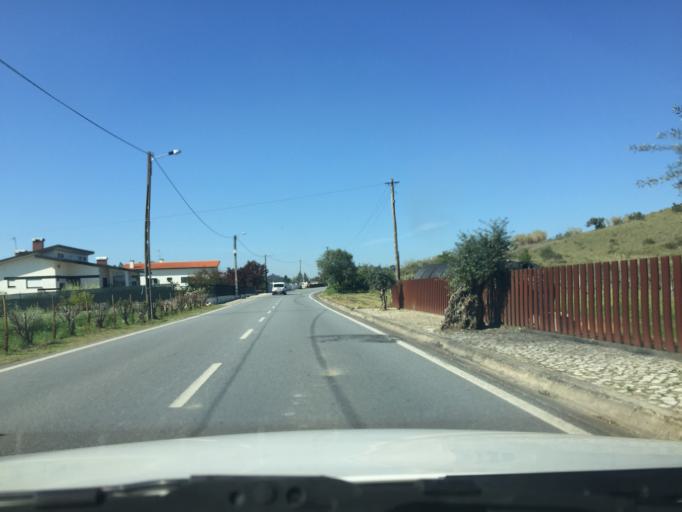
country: PT
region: Aveiro
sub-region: Anadia
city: Arcos
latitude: 40.4401
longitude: -8.4903
